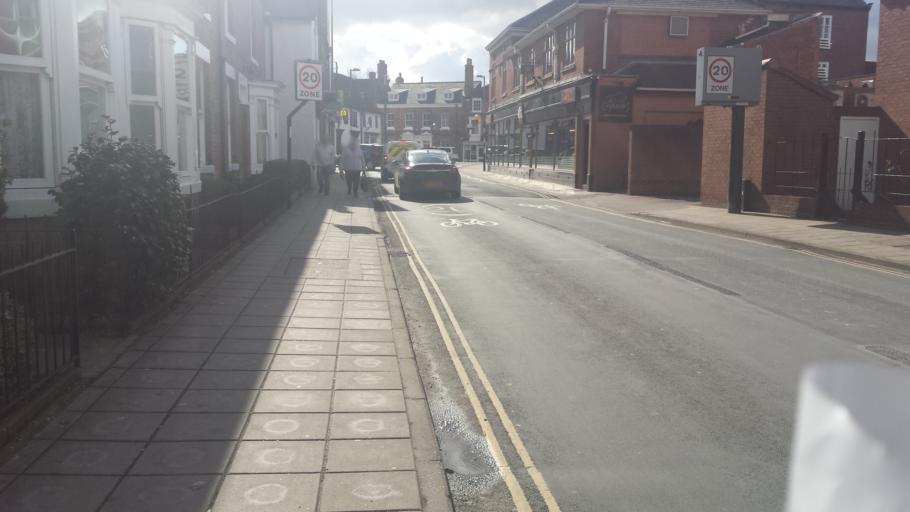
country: GB
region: England
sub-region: East Riding of Yorkshire
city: Beverley
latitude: 53.8415
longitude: -0.4255
